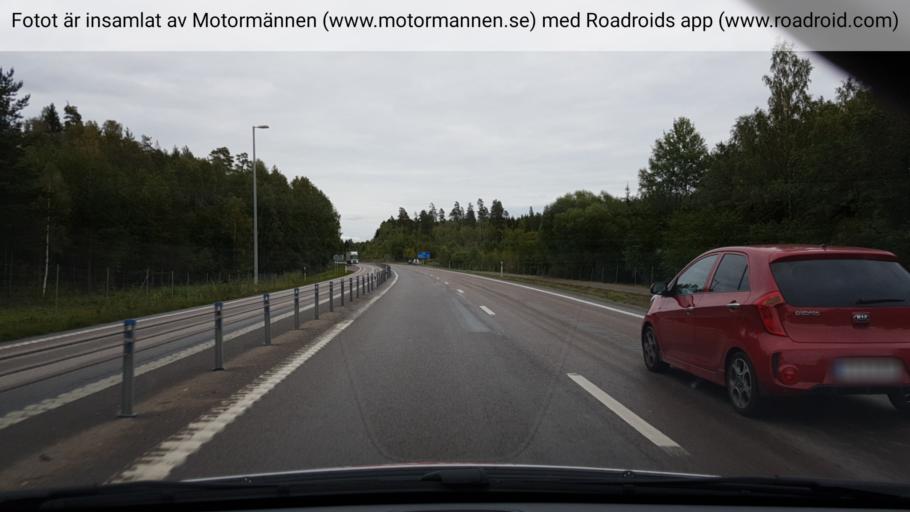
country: SE
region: Vaermland
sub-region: Karlstads Kommun
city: Valberg
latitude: 59.3682
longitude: 13.1504
